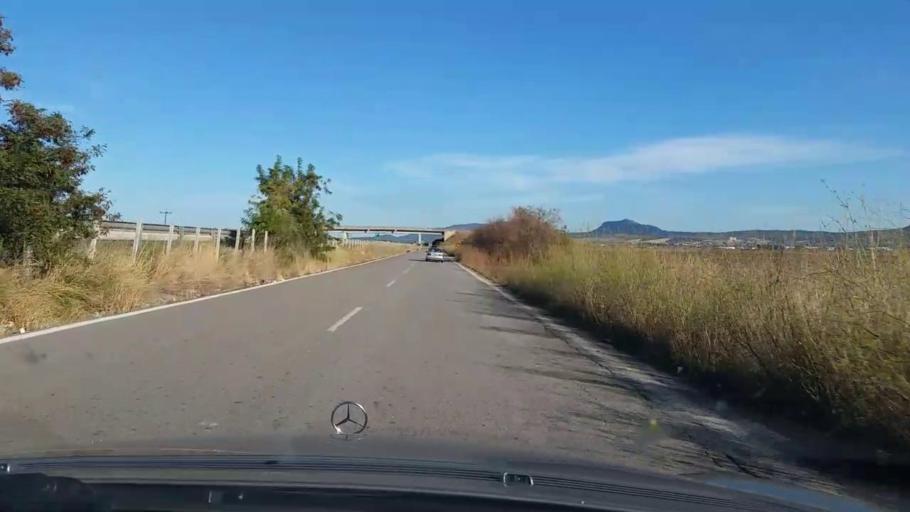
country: GR
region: Central Greece
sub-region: Nomos Voiotias
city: Thivai
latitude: 38.3683
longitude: 23.2968
